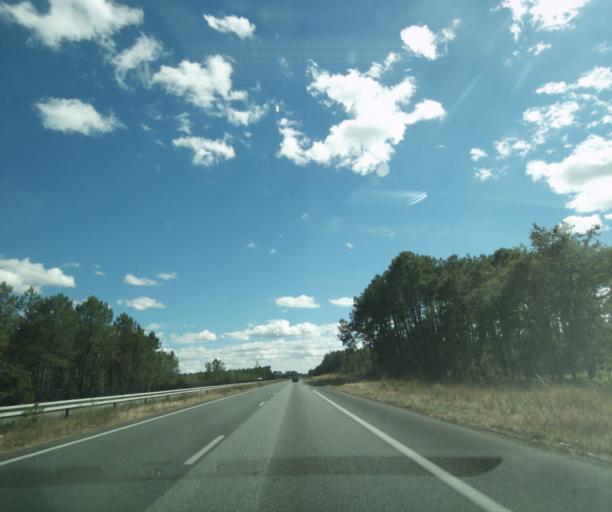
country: FR
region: Aquitaine
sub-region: Departement de la Gironde
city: Illats
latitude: 44.6282
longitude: -0.4049
